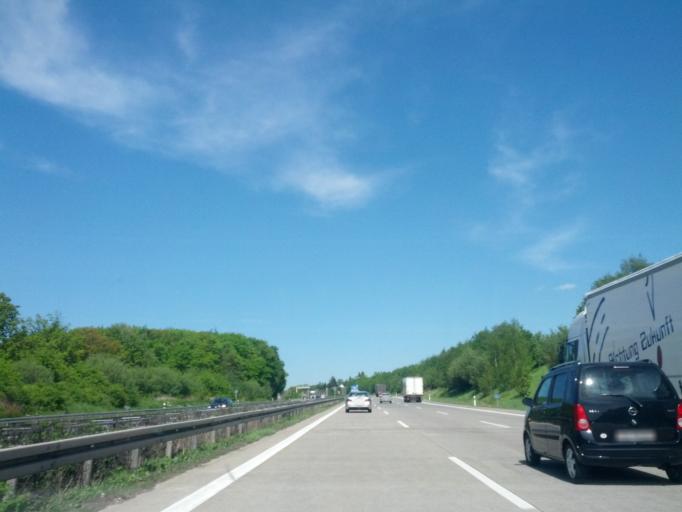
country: DE
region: Saxony
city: Chemnitz
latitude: 50.8814
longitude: 12.9234
